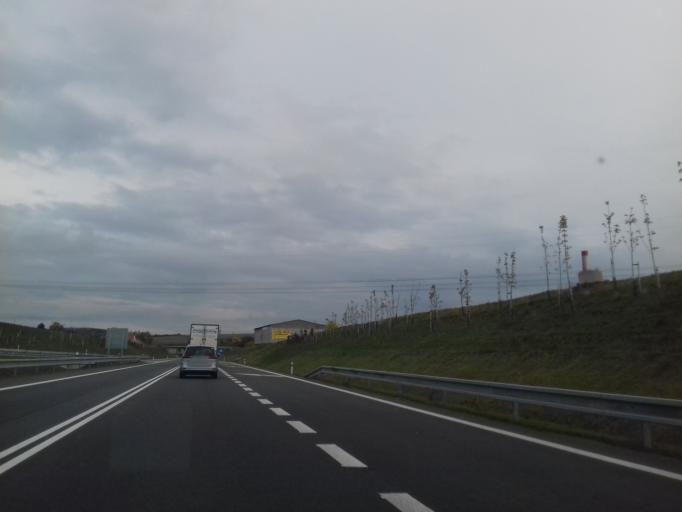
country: CZ
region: Pardubicky
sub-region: Okres Chrudim
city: Chrudim
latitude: 49.9690
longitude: 15.7996
